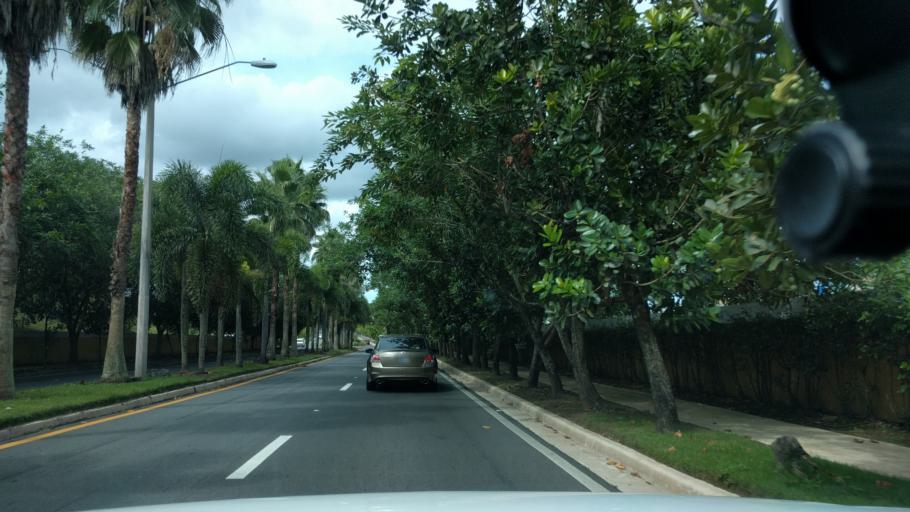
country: PR
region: Toa Alta
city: Pajaros
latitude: 18.3420
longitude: -66.2045
